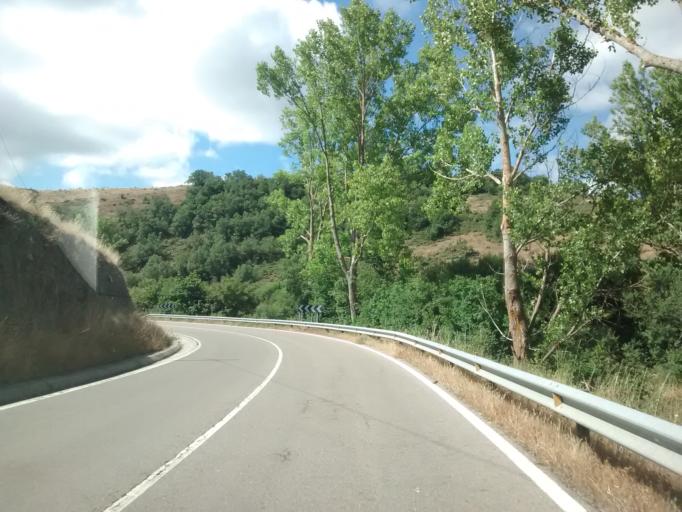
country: ES
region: Castille and Leon
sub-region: Provincia de Palencia
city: Berzosilla
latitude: 42.8742
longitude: -4.0641
